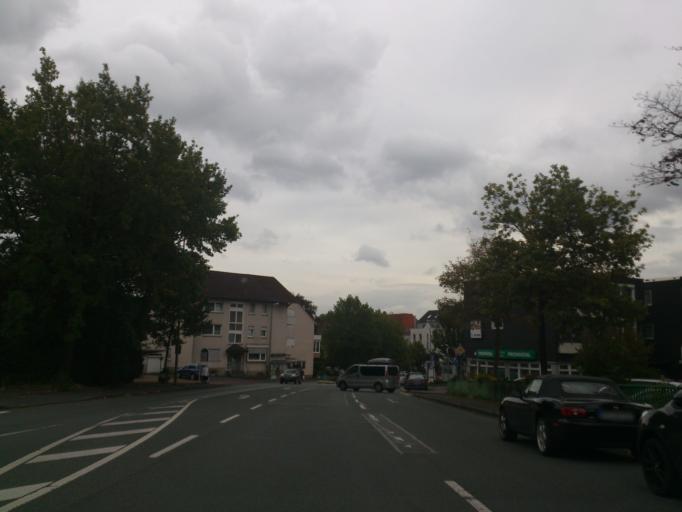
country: DE
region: North Rhine-Westphalia
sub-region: Regierungsbezirk Detmold
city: Bad Driburg
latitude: 51.7354
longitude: 9.0225
